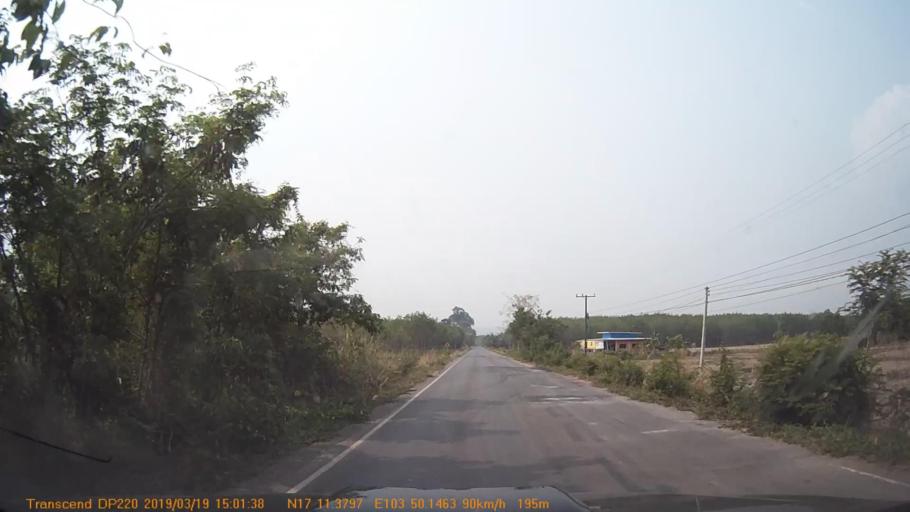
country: TH
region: Sakon Nakhon
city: Kut Bak
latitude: 17.1899
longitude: 103.8357
